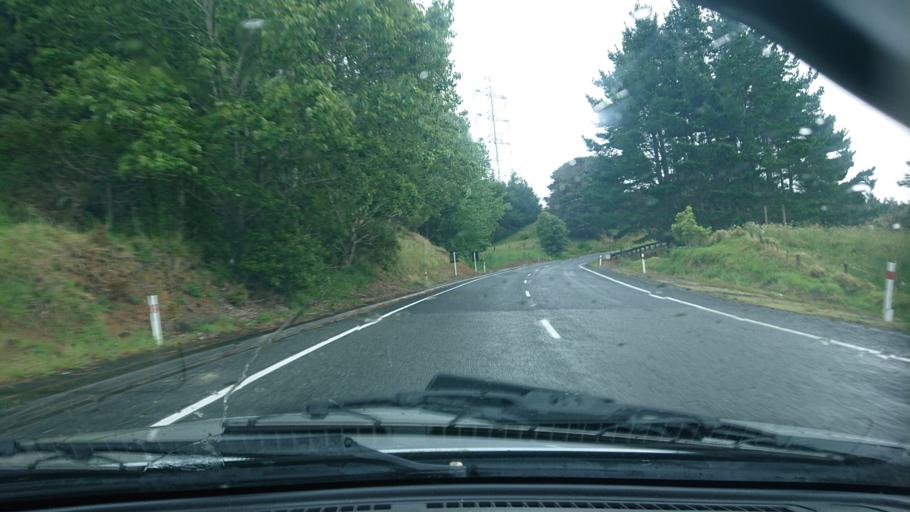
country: NZ
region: Auckland
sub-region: Auckland
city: Wellsford
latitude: -36.3432
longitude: 174.4769
